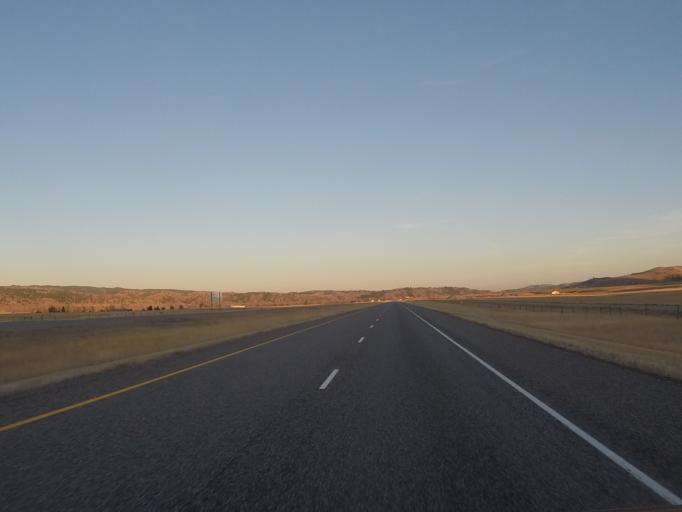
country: US
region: Montana
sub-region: Sweet Grass County
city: Big Timber
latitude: 45.7344
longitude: -109.7144
